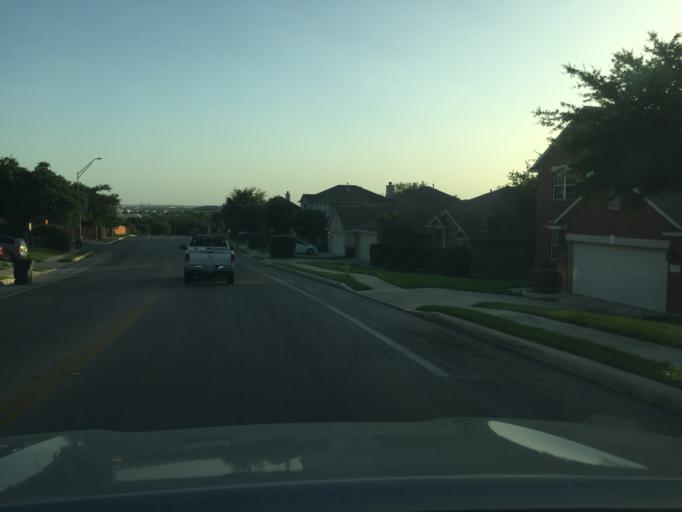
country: US
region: Texas
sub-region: Bexar County
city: Hollywood Park
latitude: 29.6342
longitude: -98.4872
